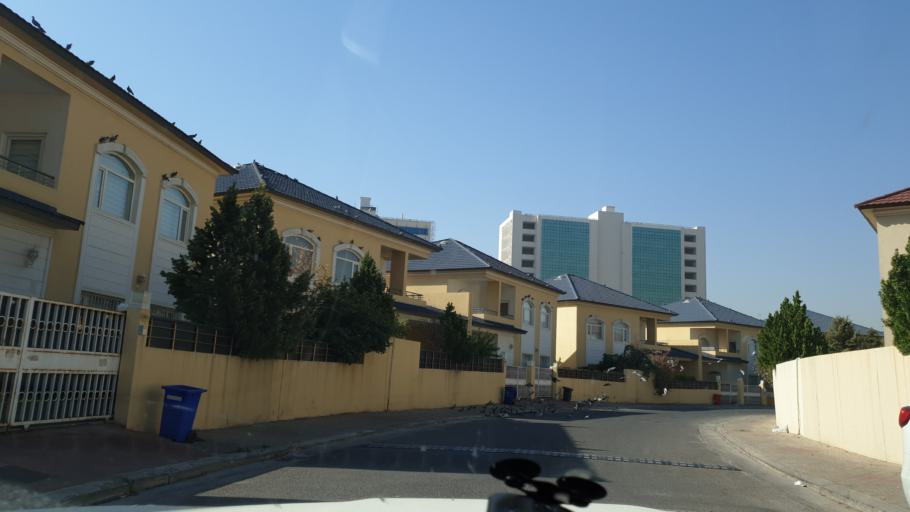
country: IQ
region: Arbil
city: Erbil
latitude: 36.1889
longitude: 43.9718
